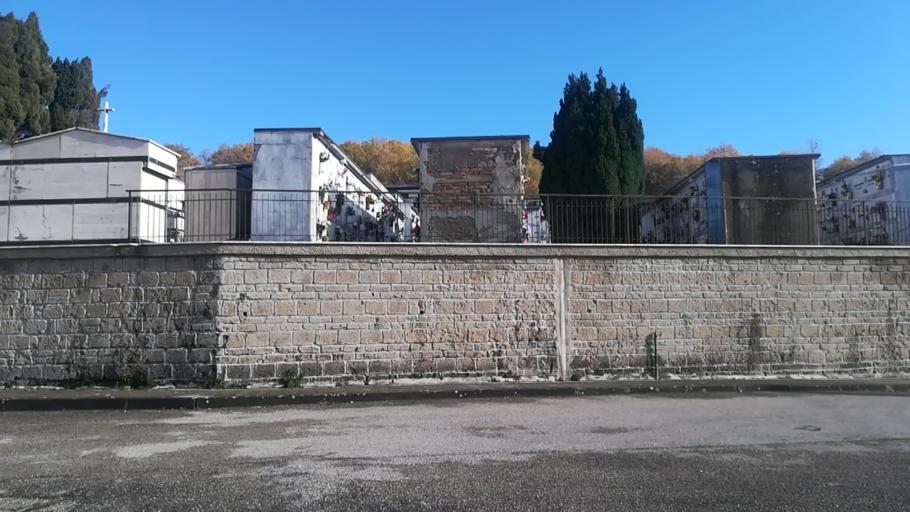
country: IT
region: Campania
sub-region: Provincia di Avellino
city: Roccabascerana
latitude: 41.0318
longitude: 14.7176
